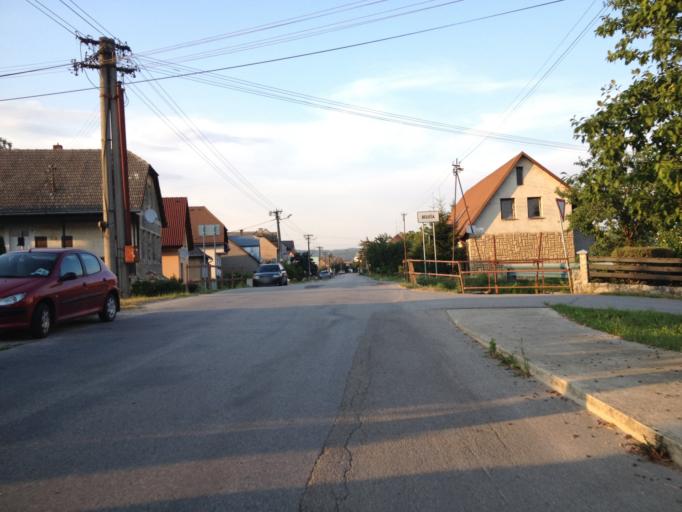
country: SK
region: Nitriansky
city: Puchov
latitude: 49.0535
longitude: 18.3135
